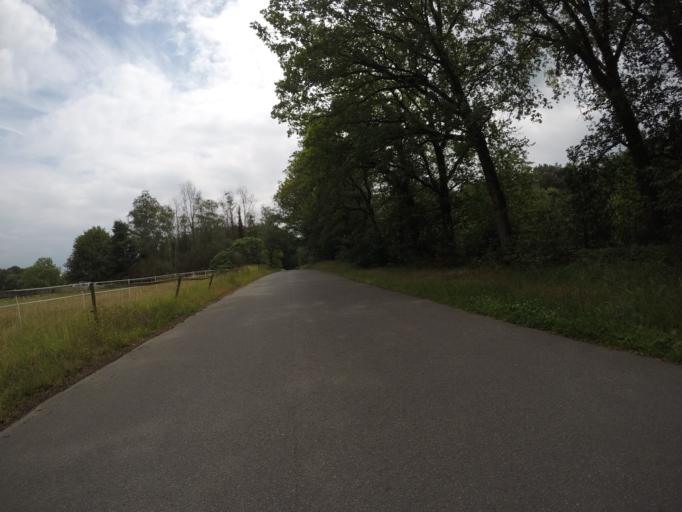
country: DE
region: North Rhine-Westphalia
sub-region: Regierungsbezirk Dusseldorf
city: Hamminkeln
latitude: 51.7327
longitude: 6.6614
